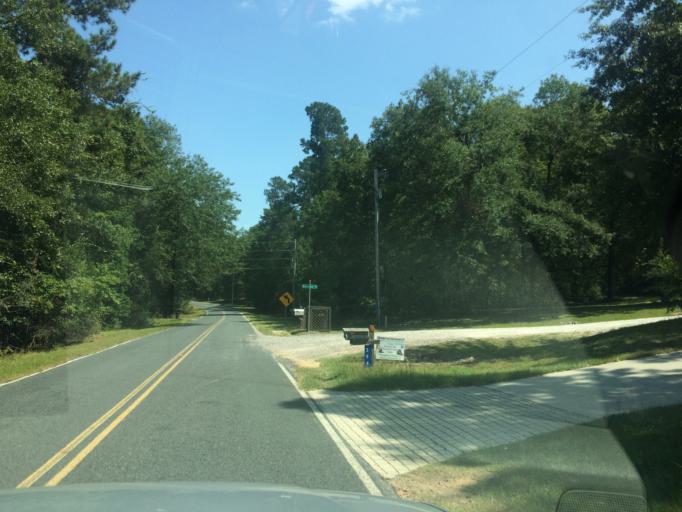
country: US
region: South Carolina
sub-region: Aiken County
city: Aiken
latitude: 33.5322
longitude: -81.5903
